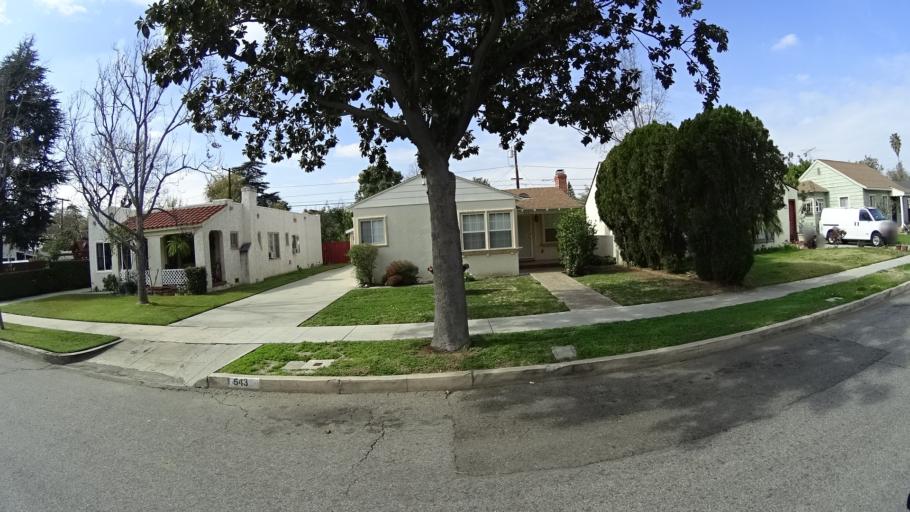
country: US
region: California
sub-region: Orange County
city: Anaheim
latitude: 33.8272
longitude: -117.9223
